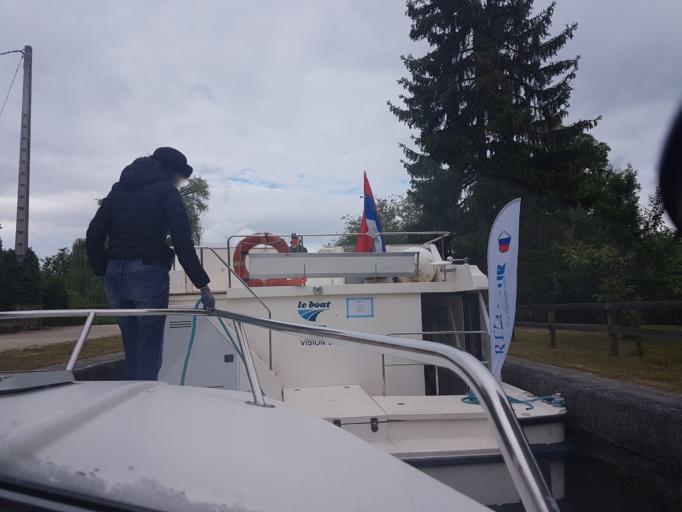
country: FR
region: Bourgogne
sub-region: Departement de l'Yonne
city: Vermenton
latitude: 47.6541
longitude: 3.6716
